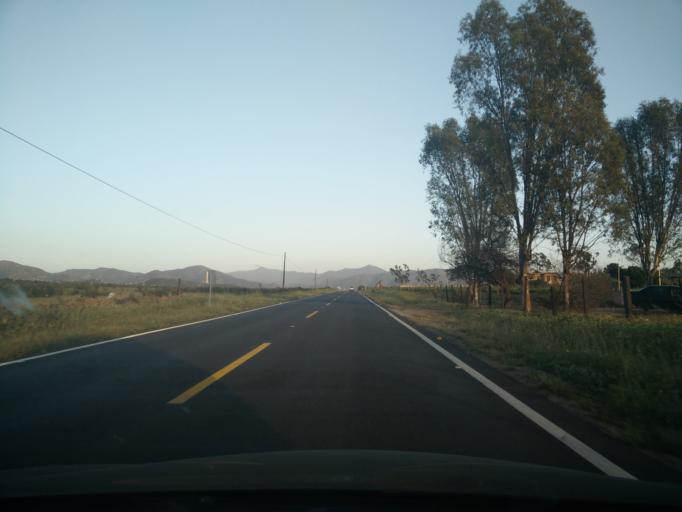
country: MX
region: Baja California
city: El Sauzal
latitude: 32.0042
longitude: -116.6728
